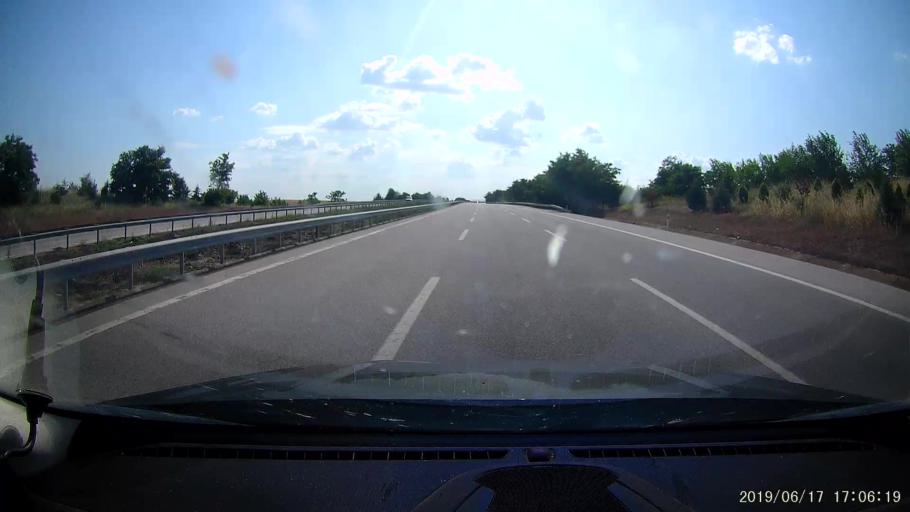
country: TR
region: Edirne
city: Edirne
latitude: 41.6621
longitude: 26.6743
